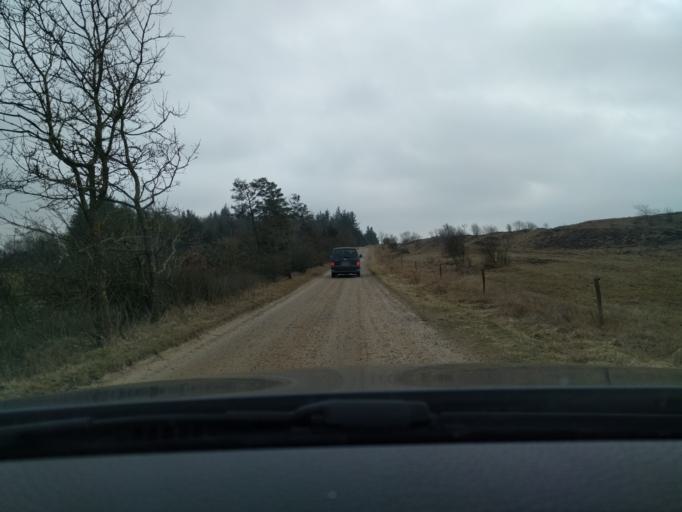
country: DK
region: Central Jutland
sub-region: Skive Kommune
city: Skive
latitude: 56.5155
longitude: 8.9521
